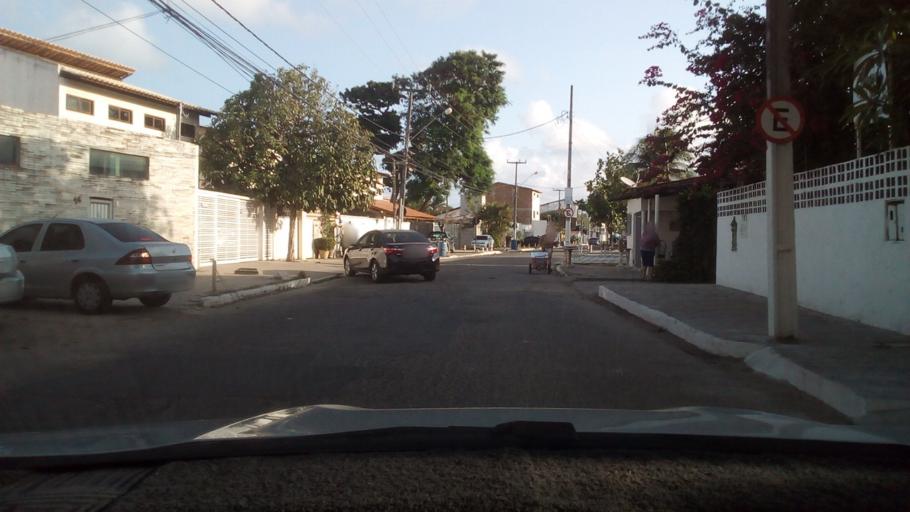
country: BR
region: Paraiba
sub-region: Cabedelo
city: Cabedelo
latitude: -7.0213
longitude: -34.8303
